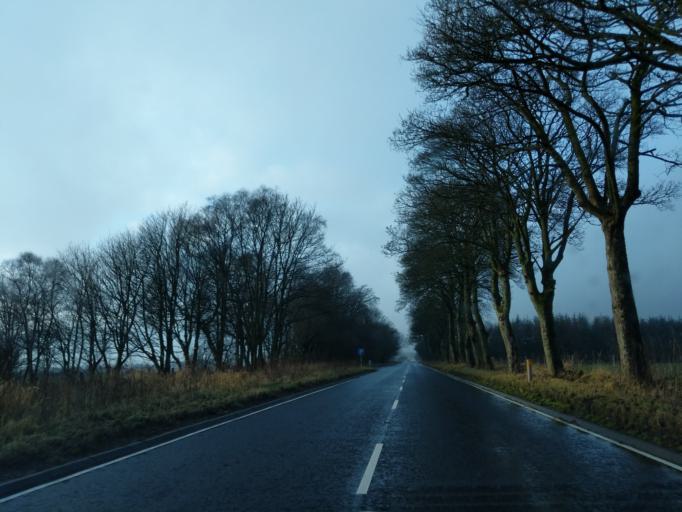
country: GB
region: Scotland
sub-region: Perth and Kinross
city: Kinross
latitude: 56.2023
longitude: -3.4885
